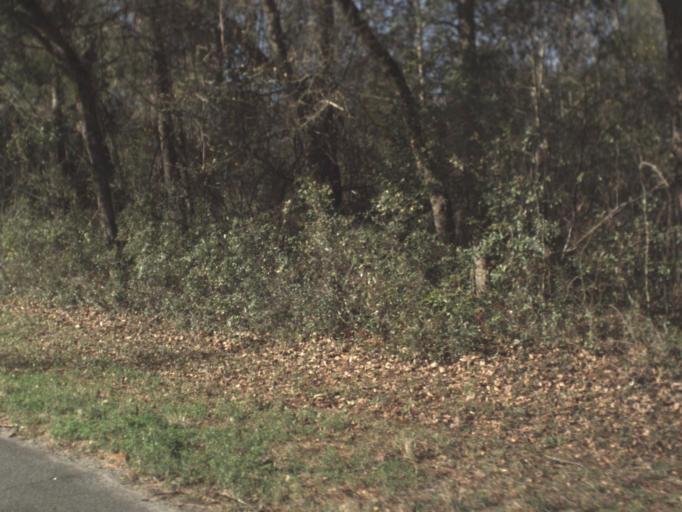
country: US
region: Georgia
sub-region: Brooks County
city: Quitman
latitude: 30.5785
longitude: -83.6370
